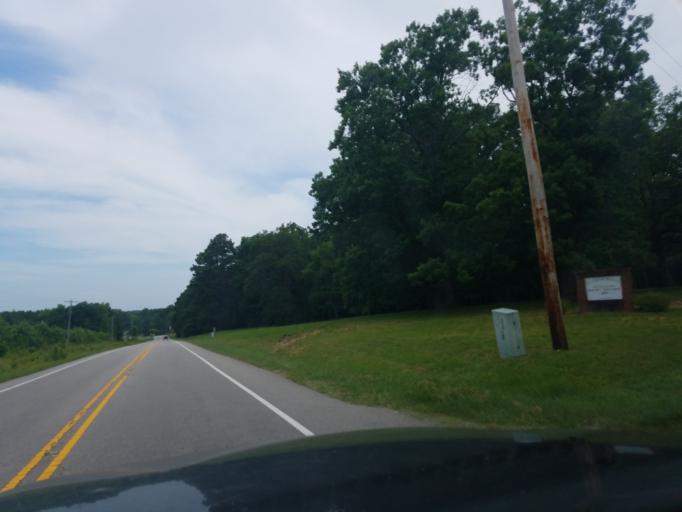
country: US
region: North Carolina
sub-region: Durham County
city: Durham
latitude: 36.1220
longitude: -78.9382
